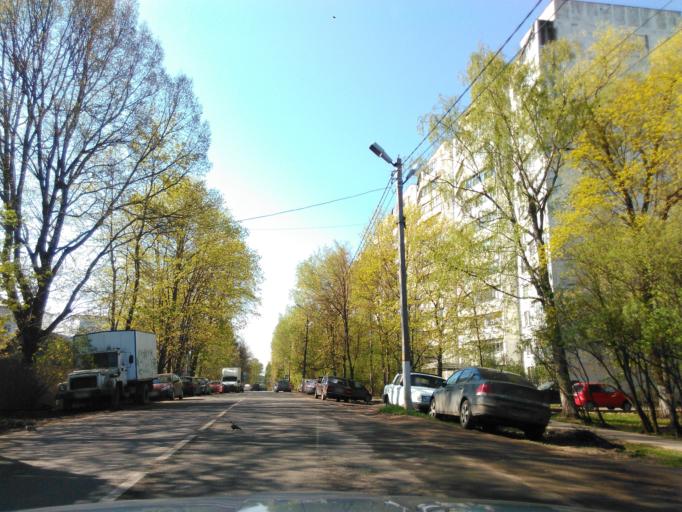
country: RU
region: Moskovskaya
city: Skhodnya
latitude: 55.9448
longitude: 37.2996
